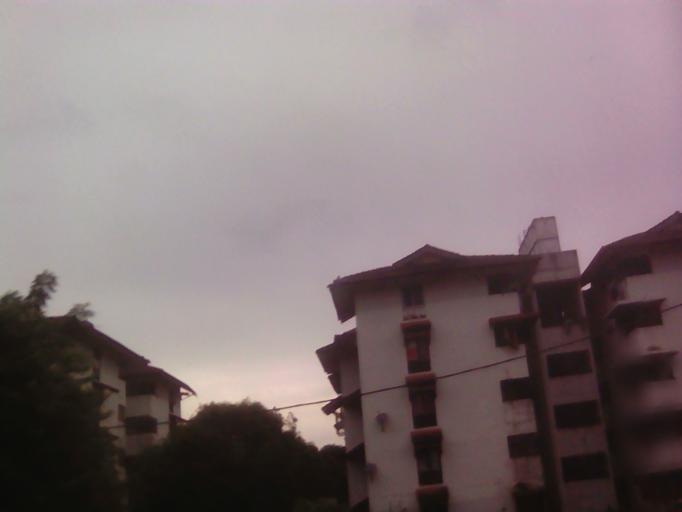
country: MY
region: Penang
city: Perai
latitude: 5.4017
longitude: 100.3975
